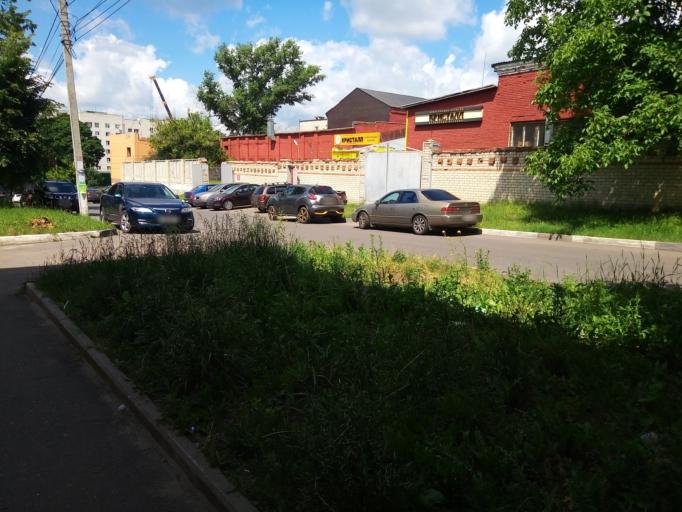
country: RU
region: Kursk
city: Kursk
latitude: 51.7442
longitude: 36.1826
